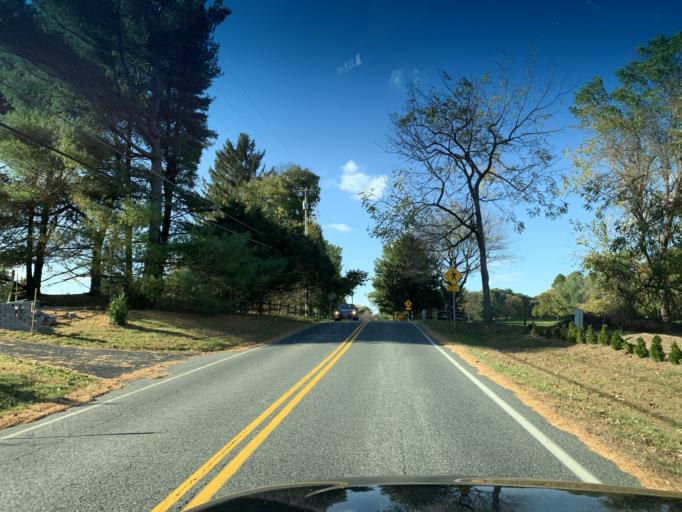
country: US
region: Maryland
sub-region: Harford County
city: Bel Air South
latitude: 39.5163
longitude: -76.2972
